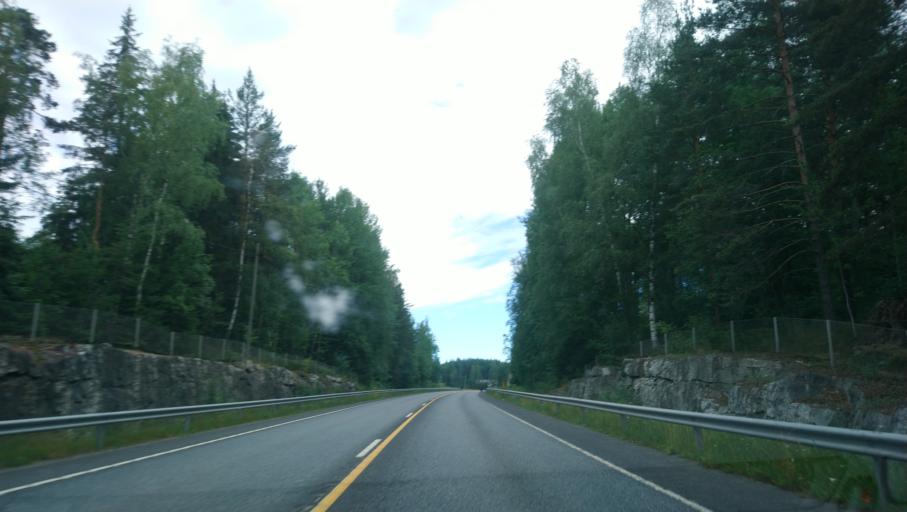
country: FI
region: Uusimaa
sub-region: Porvoo
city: Porvoo
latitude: 60.4189
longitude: 25.5791
